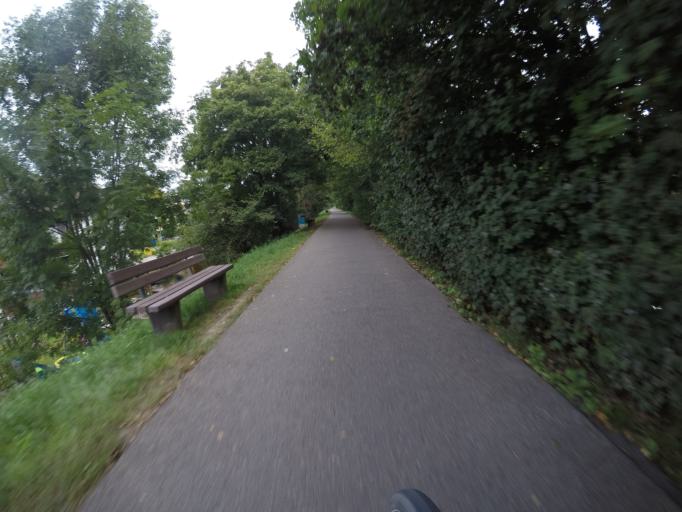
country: DE
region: Baden-Wuerttemberg
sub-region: Regierungsbezirk Stuttgart
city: Stuttgart Muehlhausen
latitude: 48.8763
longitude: 9.2757
